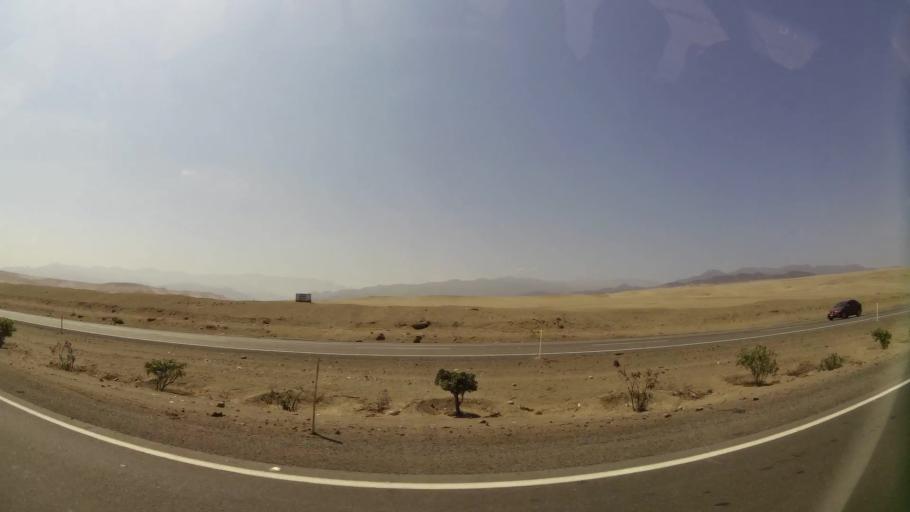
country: PE
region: Lima
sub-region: Provincia de Canete
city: Asia
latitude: -12.8294
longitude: -76.5289
